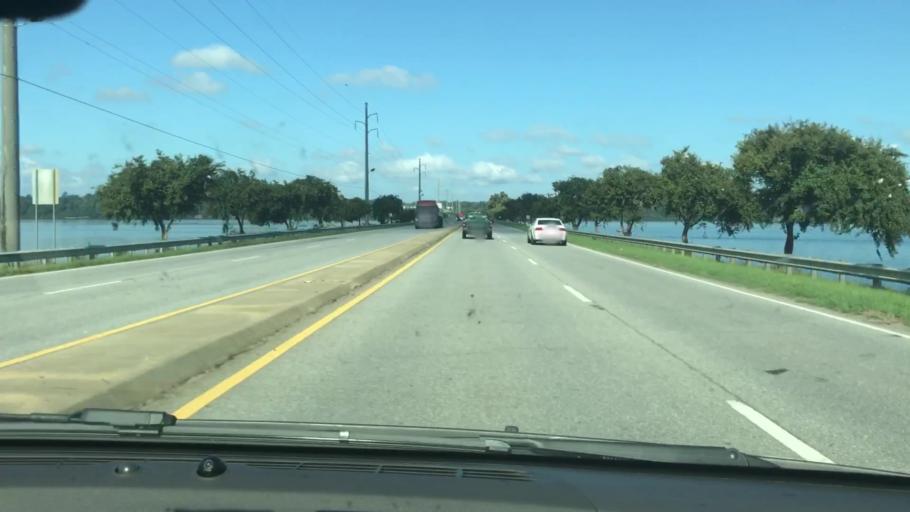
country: US
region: Georgia
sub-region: Quitman County
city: Georgetown
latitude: 31.8887
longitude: -85.1137
